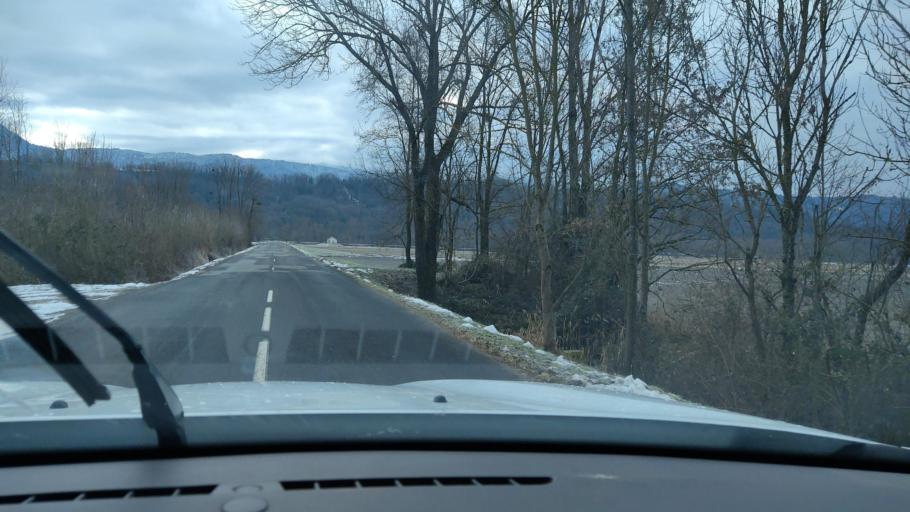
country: FR
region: Rhone-Alpes
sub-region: Departement de la Savoie
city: Coise-Saint-Jean-Pied-Gauthier
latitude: 45.5457
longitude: 6.1311
